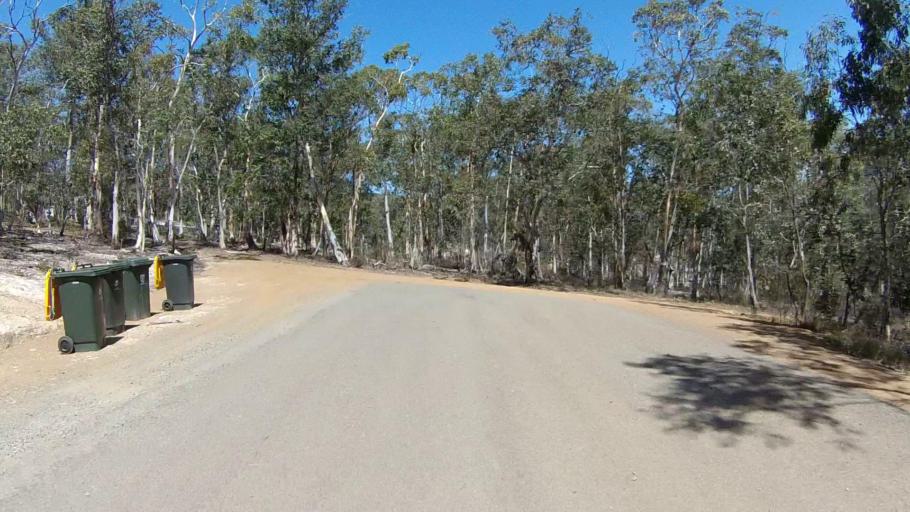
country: AU
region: Tasmania
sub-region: Clarence
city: Sandford
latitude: -42.9606
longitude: 147.4826
